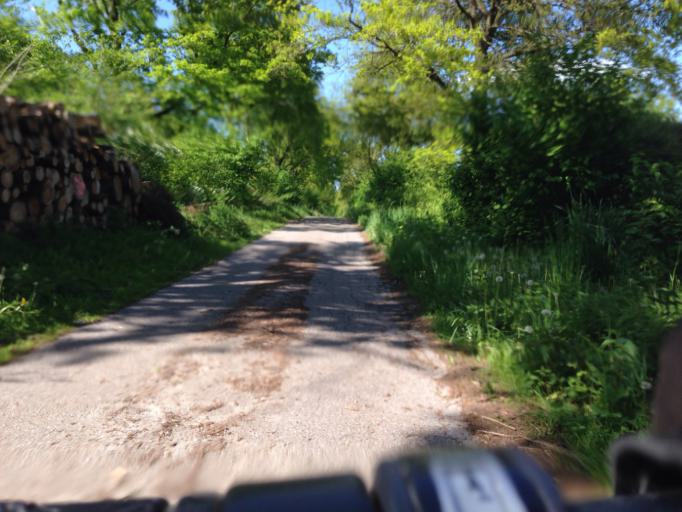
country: DE
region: Schleswig-Holstein
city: Braak
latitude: 53.6284
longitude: 10.2293
